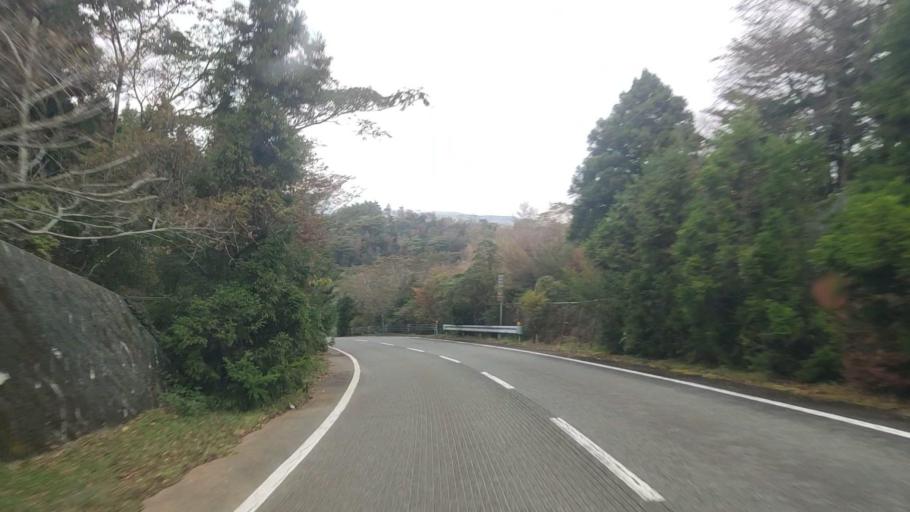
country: JP
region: Shizuoka
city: Heda
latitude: 34.8924
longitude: 138.8440
